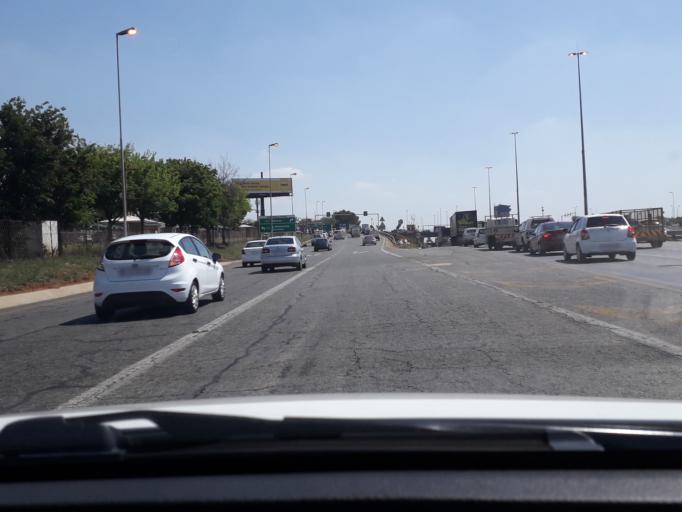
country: ZA
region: Gauteng
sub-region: City of Johannesburg Metropolitan Municipality
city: Modderfontein
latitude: -26.1549
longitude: 28.1659
